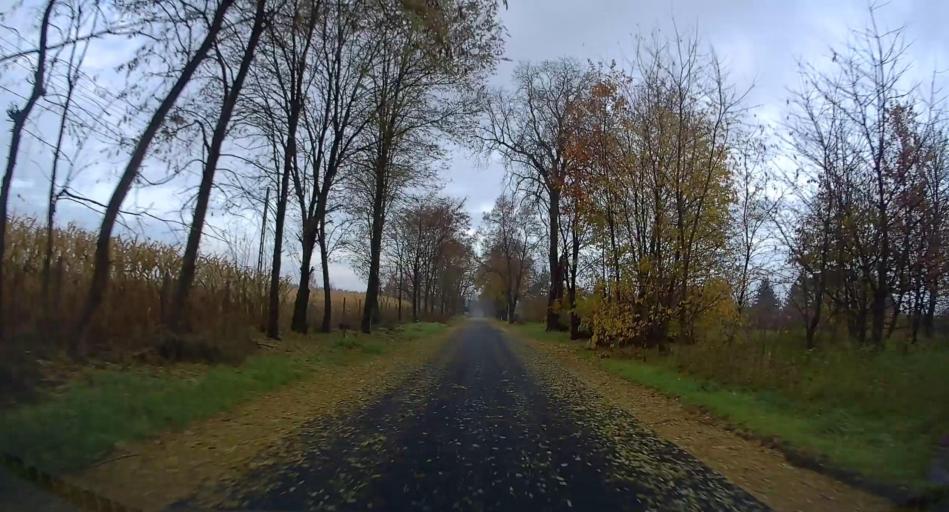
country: PL
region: Lodz Voivodeship
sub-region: Powiat skierniewicki
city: Kowiesy
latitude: 51.9249
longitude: 20.4076
